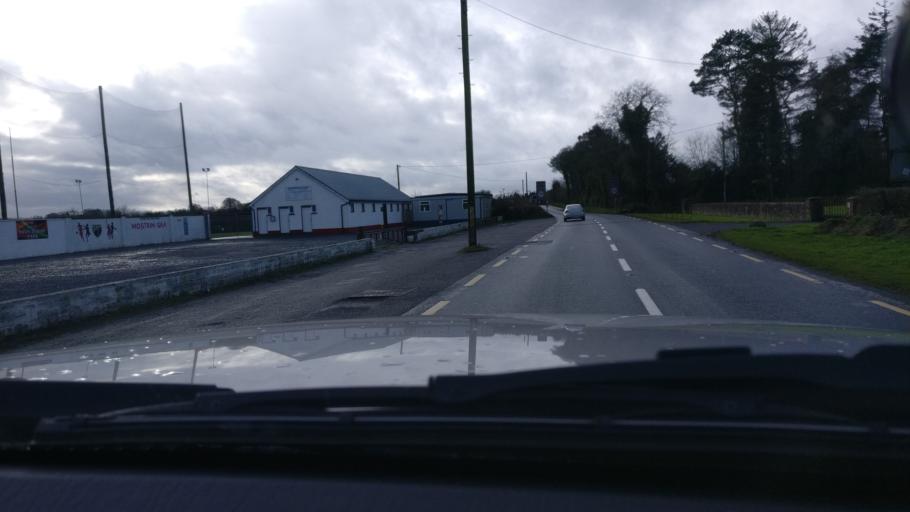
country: IE
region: Leinster
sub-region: An Longfort
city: Edgeworthstown
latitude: 53.6940
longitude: -7.6164
